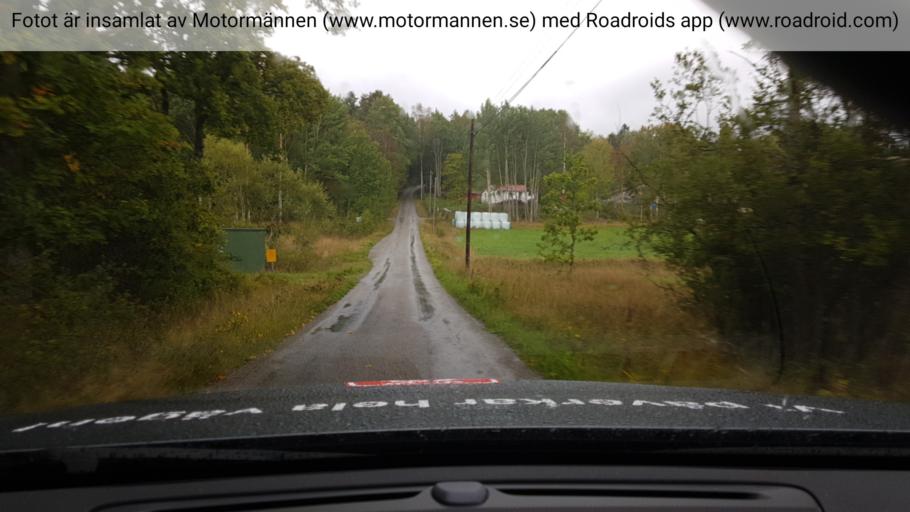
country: SE
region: Stockholm
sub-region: Haninge Kommun
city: Jordbro
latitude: 59.0128
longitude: 18.1168
